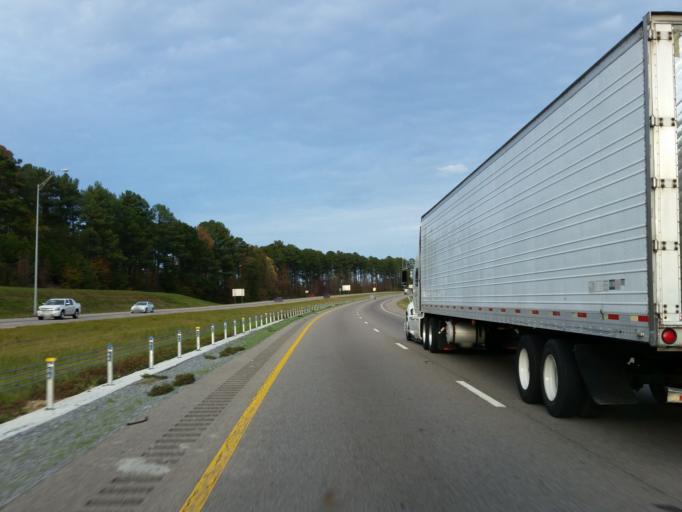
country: US
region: Mississippi
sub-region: Lauderdale County
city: Meridian
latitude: 32.3714
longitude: -88.6682
